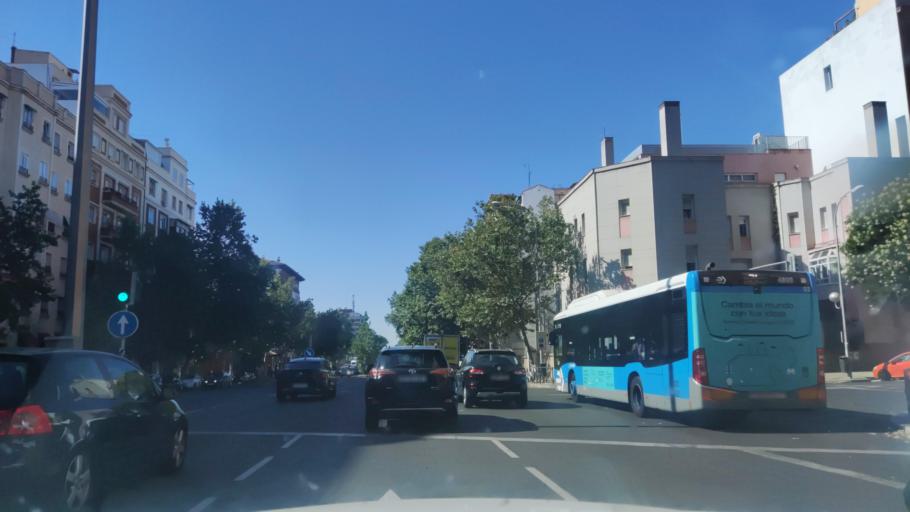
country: ES
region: Madrid
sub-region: Provincia de Madrid
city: Salamanca
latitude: 40.4247
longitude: -3.6688
